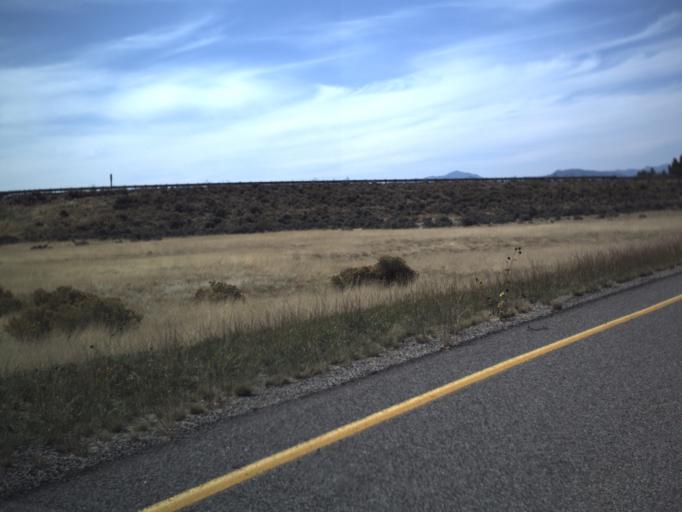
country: US
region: Utah
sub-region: Iron County
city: Enoch
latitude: 37.8043
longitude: -112.9448
